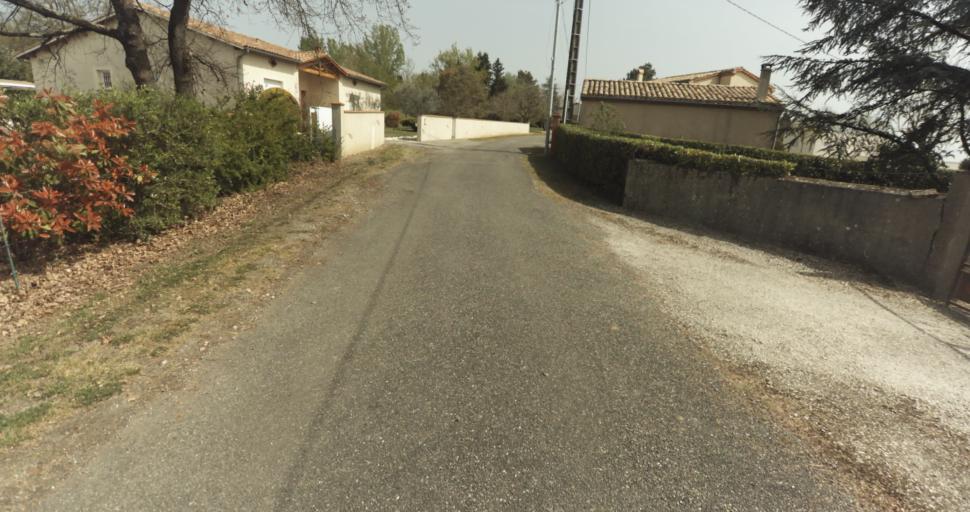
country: FR
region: Midi-Pyrenees
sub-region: Departement du Tarn-et-Garonne
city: Moissac
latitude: 44.1050
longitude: 1.0766
